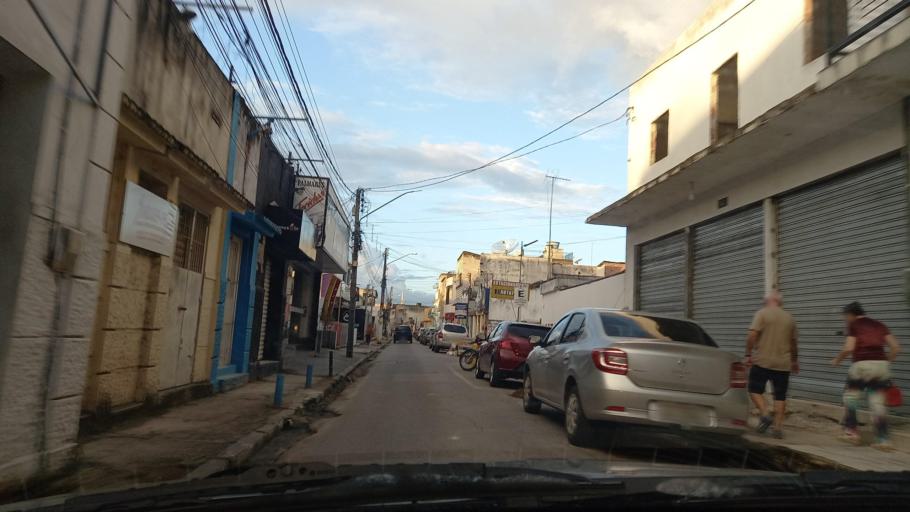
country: BR
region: Pernambuco
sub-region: Palmares
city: Palmares
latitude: -8.6845
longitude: -35.5903
